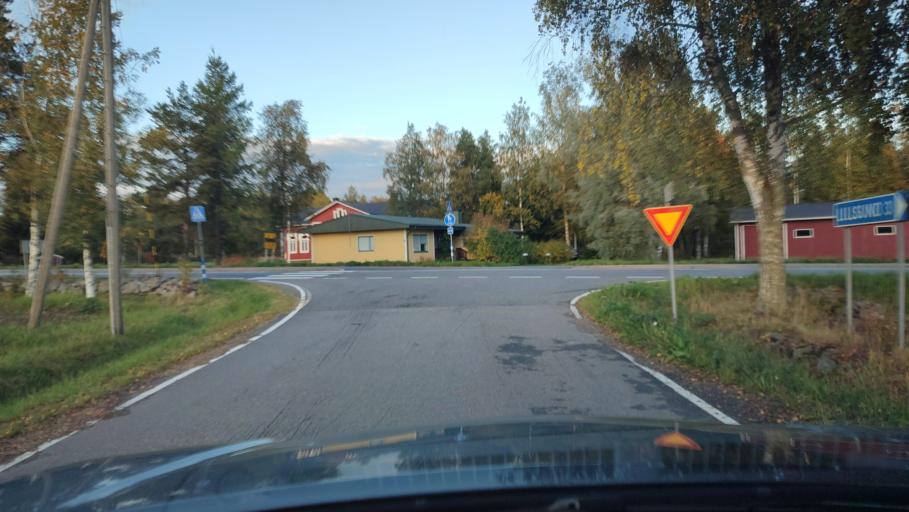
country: FI
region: Ostrobothnia
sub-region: Sydosterbotten
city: Kristinestad
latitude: 62.2449
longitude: 21.5205
